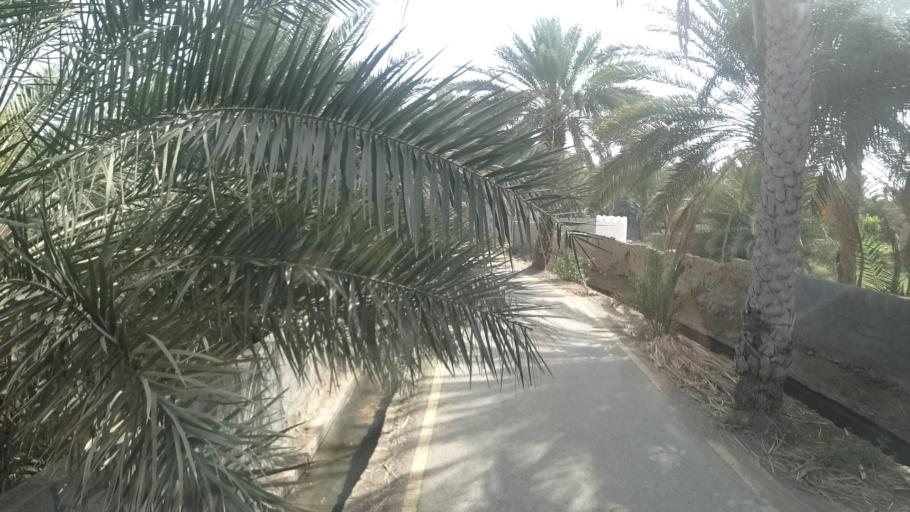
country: OM
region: Ash Sharqiyah
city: Ibra'
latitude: 22.7114
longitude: 58.1713
